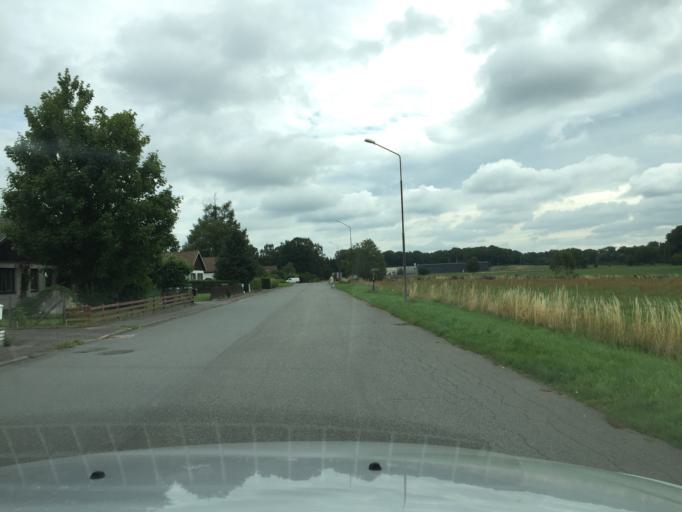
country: SE
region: Skane
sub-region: Hassleholms Kommun
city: Sosdala
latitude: 56.0349
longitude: 13.6819
